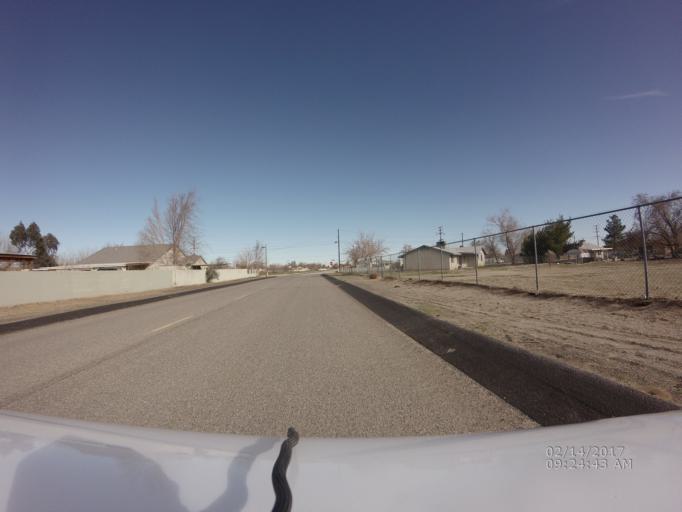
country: US
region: California
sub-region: Los Angeles County
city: Littlerock
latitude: 34.5718
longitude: -117.9476
